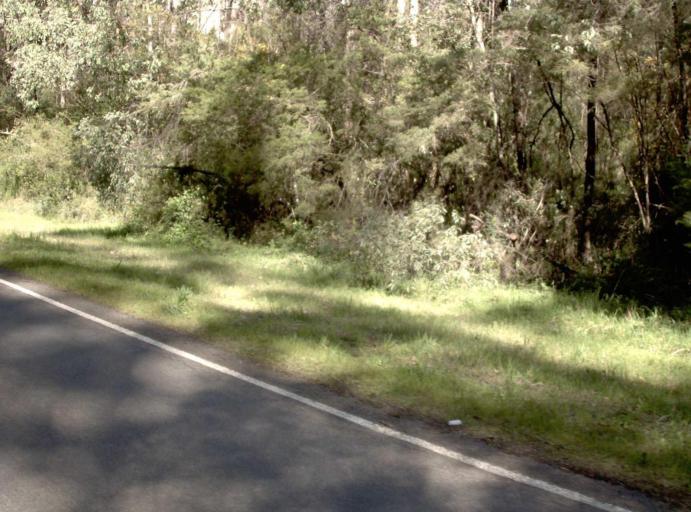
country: AU
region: Victoria
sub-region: Yarra Ranges
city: Millgrove
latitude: -37.8759
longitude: 145.8347
